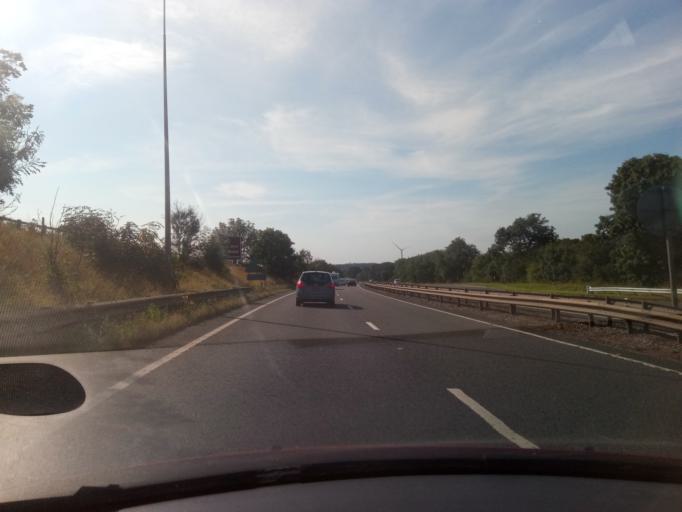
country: GB
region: England
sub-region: Hartlepool
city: Elwick
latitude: 54.6665
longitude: -1.3004
